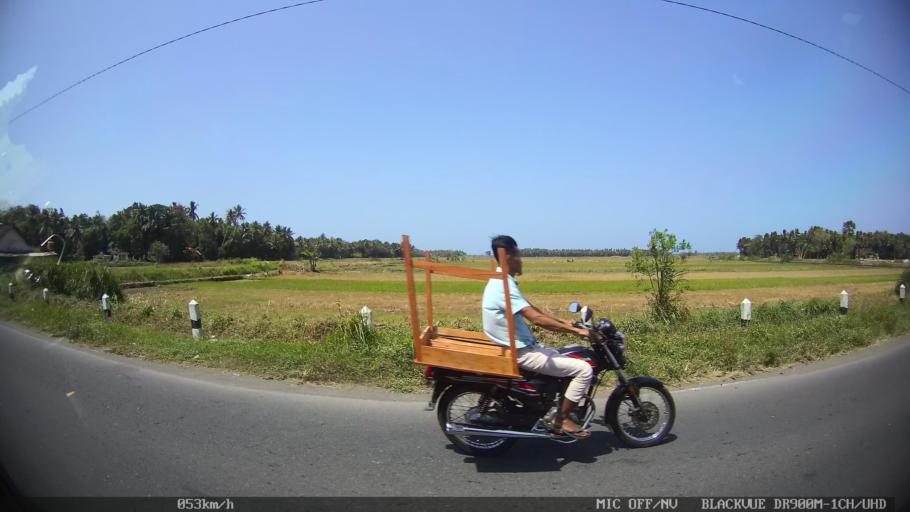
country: ID
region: Daerah Istimewa Yogyakarta
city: Srandakan
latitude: -7.9515
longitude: 110.2079
